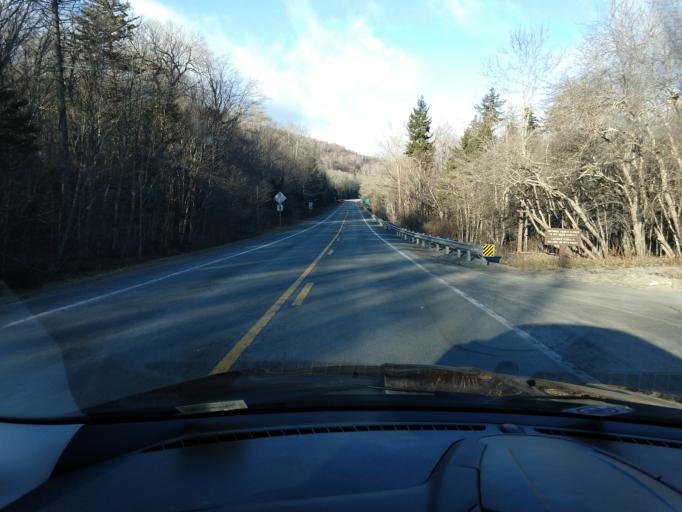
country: US
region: West Virginia
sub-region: Randolph County
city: Elkins
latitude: 38.6000
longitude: -79.8512
